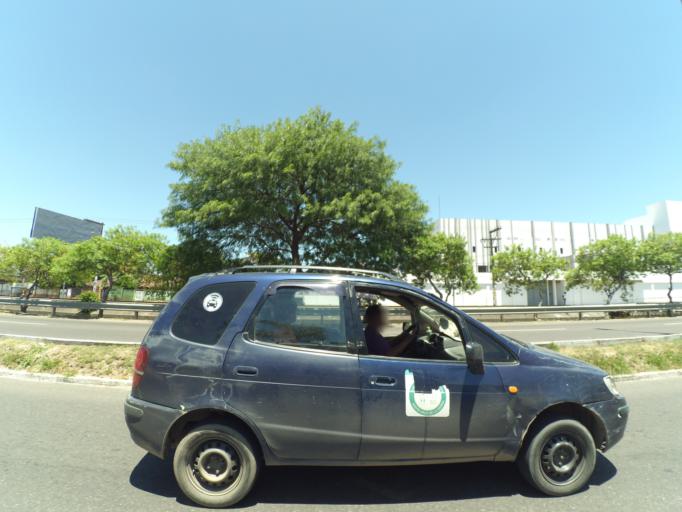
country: BO
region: Santa Cruz
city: Santa Cruz de la Sierra
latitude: -17.7888
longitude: -63.1945
